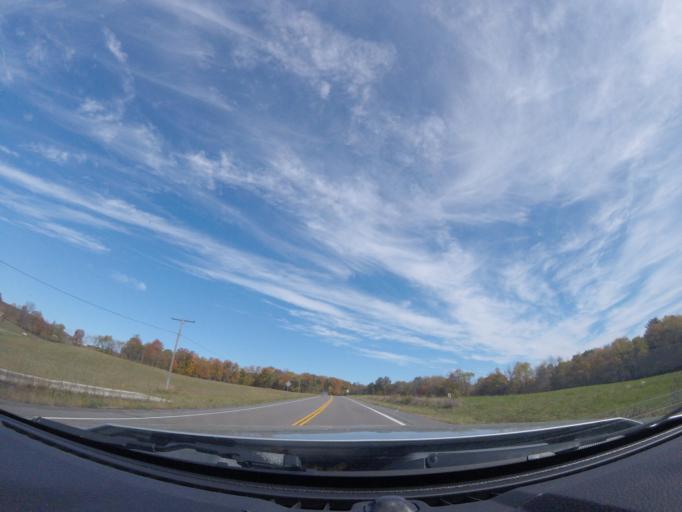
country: US
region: New York
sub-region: Cortland County
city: Cortland West
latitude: 42.5663
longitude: -76.2606
